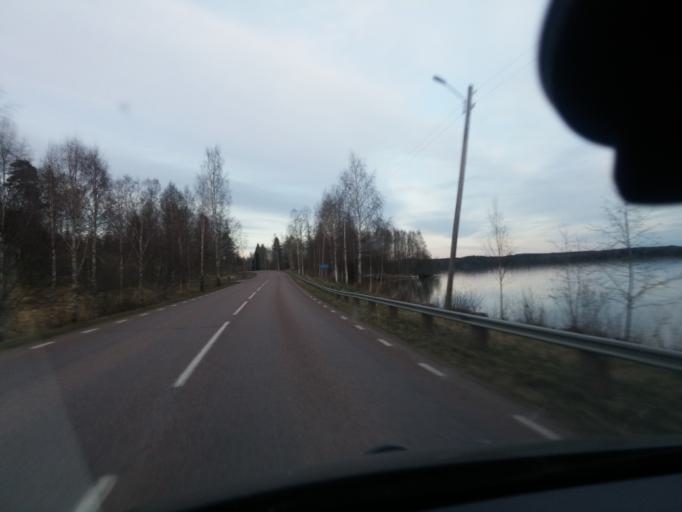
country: SE
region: Dalarna
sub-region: Faluns Kommun
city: Bjursas
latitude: 60.7205
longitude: 15.3362
